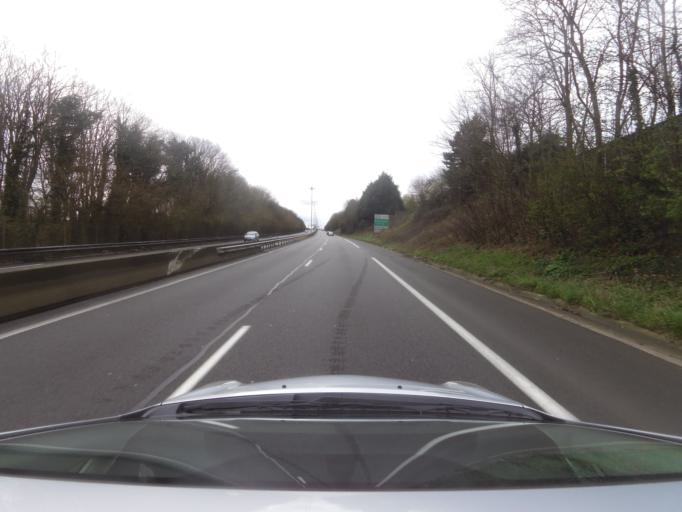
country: FR
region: Nord-Pas-de-Calais
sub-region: Departement du Pas-de-Calais
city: Wimille
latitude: 50.7599
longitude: 1.6332
